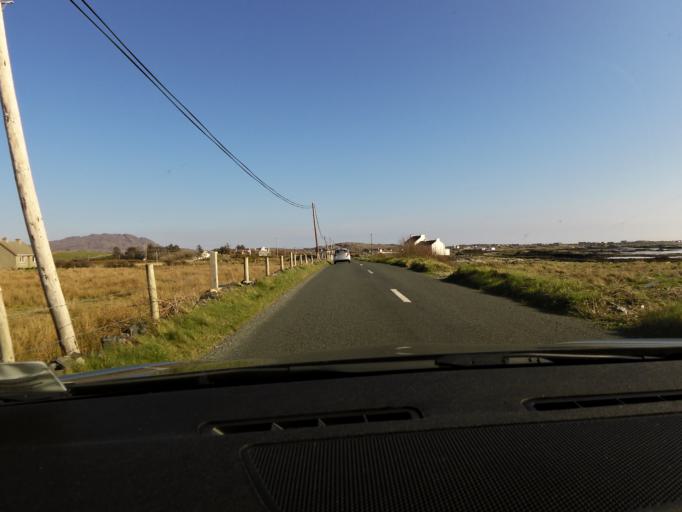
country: IE
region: Connaught
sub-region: County Galway
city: Clifden
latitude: 53.4112
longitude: -10.0395
